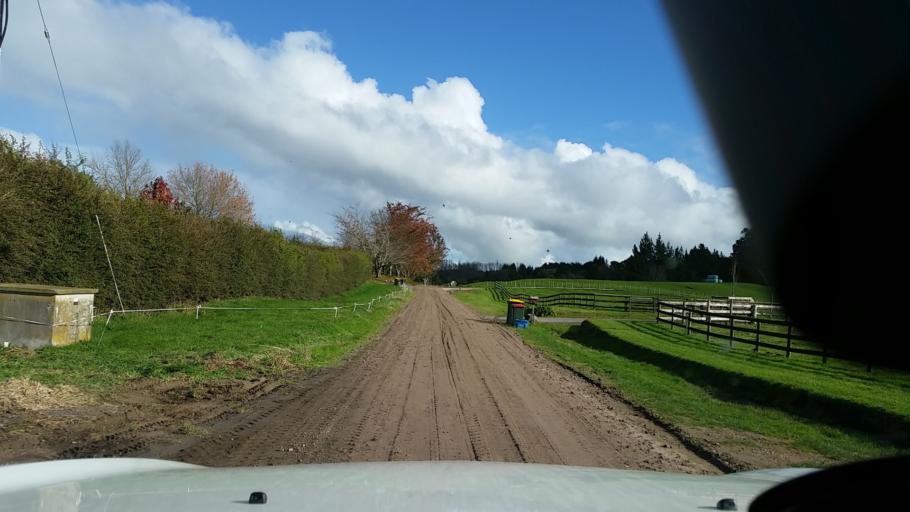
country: NZ
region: Bay of Plenty
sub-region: Rotorua District
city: Rotorua
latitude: -38.0377
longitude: 176.1943
